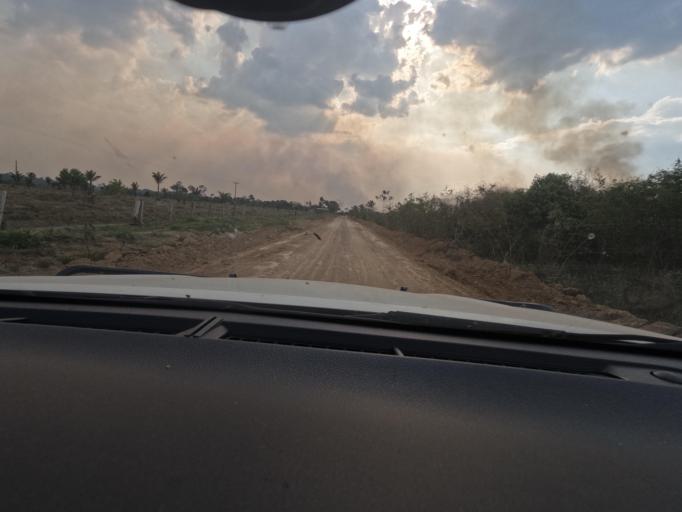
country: BR
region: Rondonia
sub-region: Porto Velho
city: Porto Velho
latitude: -8.6379
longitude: -63.1640
